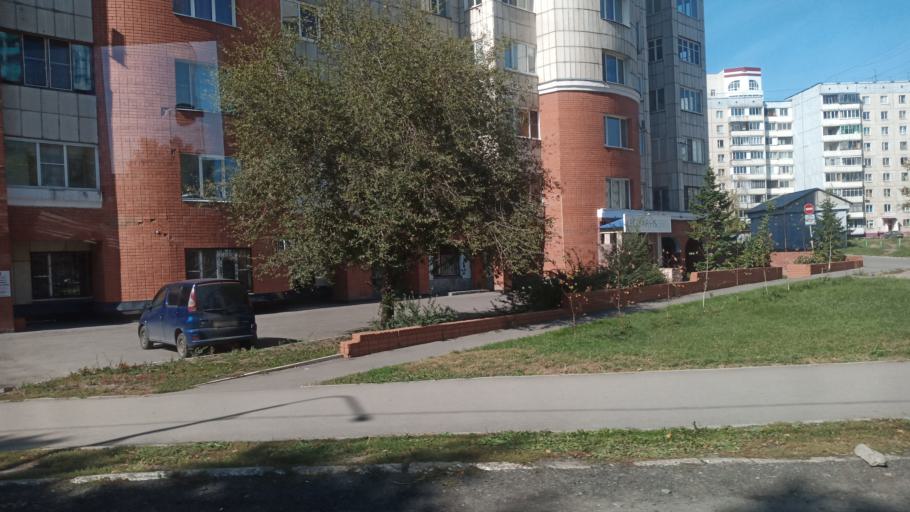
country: RU
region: Altai Krai
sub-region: Gorod Barnaulskiy
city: Barnaul
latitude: 53.3349
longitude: 83.7718
